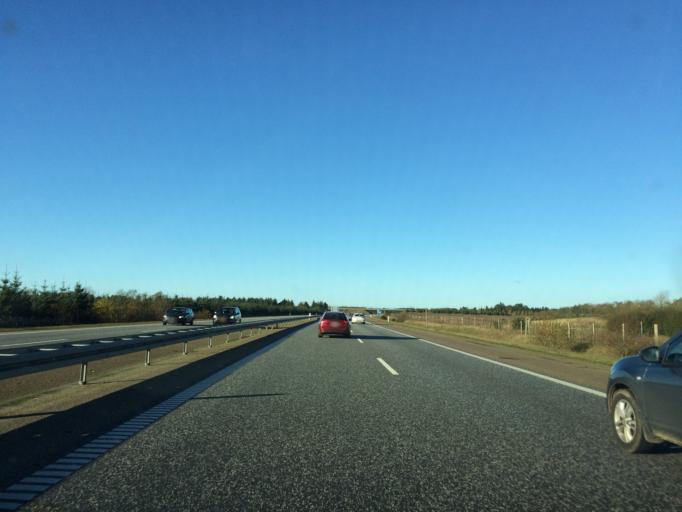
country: DK
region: Central Jutland
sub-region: Herning Kommune
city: Lind
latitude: 56.0240
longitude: 9.0107
